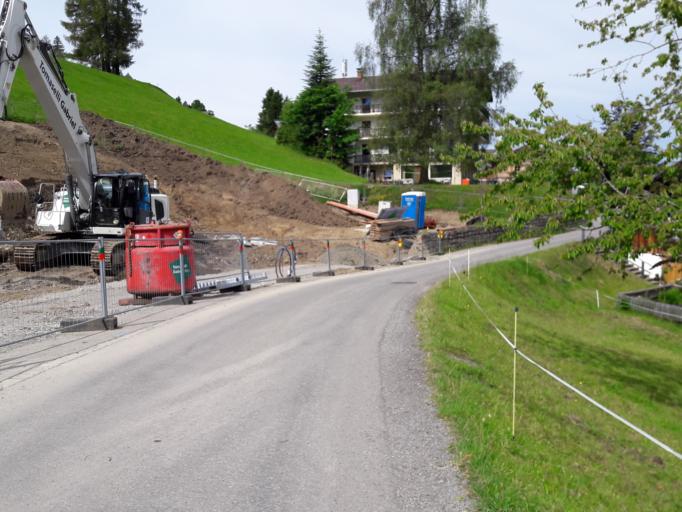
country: AT
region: Vorarlberg
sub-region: Politischer Bezirk Bludenz
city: Raggal
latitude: 47.2104
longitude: 9.8348
